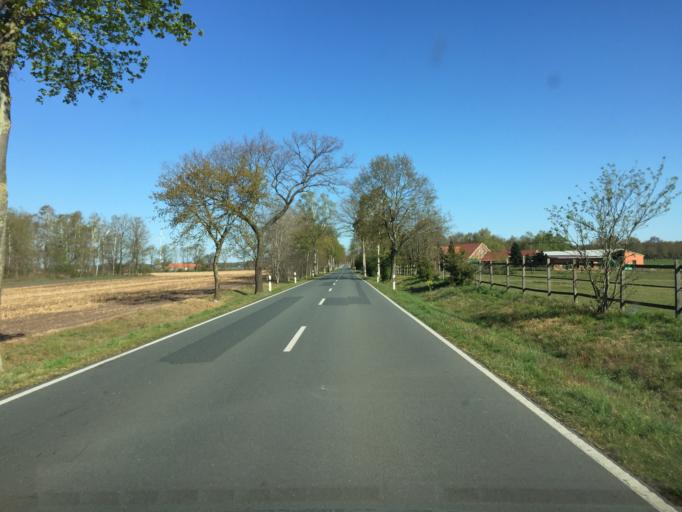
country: DE
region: Lower Saxony
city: Varrel
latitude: 52.6369
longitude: 8.7374
